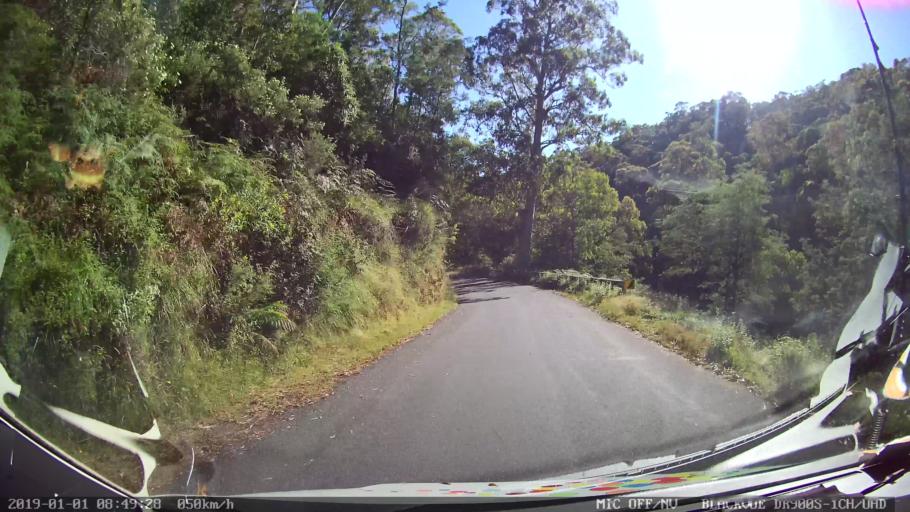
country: AU
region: New South Wales
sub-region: Snowy River
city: Jindabyne
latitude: -36.2822
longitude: 148.2000
